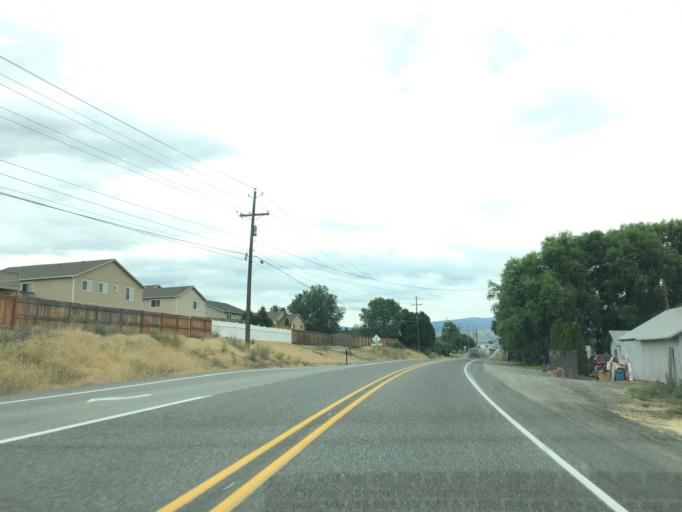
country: US
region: Washington
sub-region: Chelan County
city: Sunnyslope
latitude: 47.4761
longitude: -120.3005
